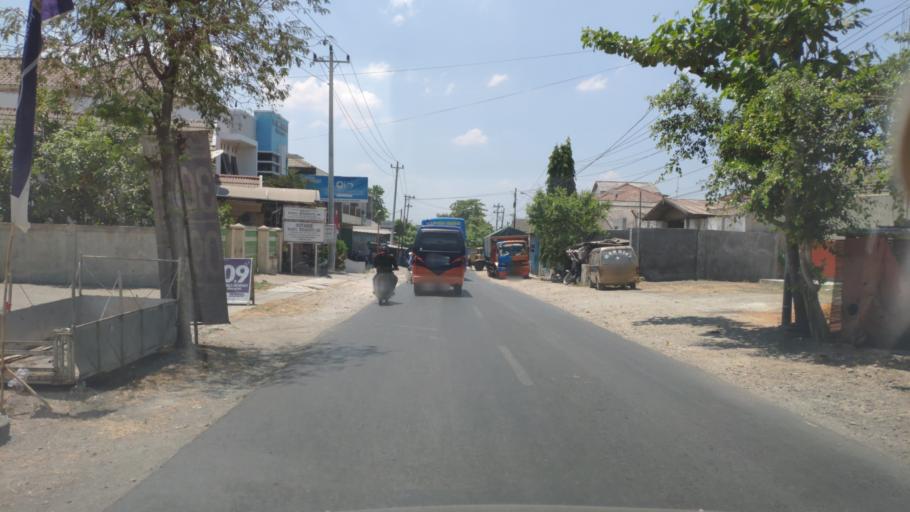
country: ID
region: Central Java
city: Tambakkromo
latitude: -7.1505
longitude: 111.5793
